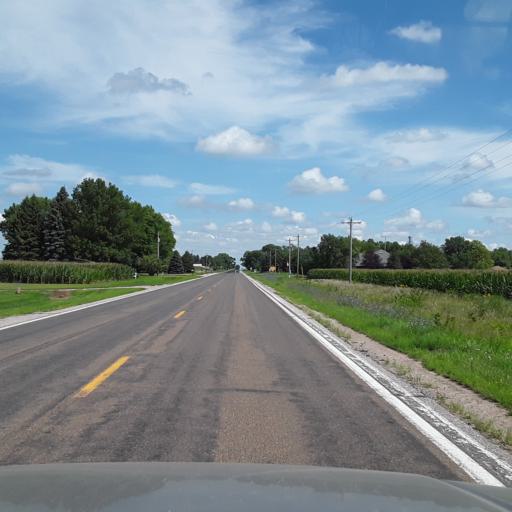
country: US
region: Nebraska
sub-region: Polk County
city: Osceola
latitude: 41.0213
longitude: -97.4062
